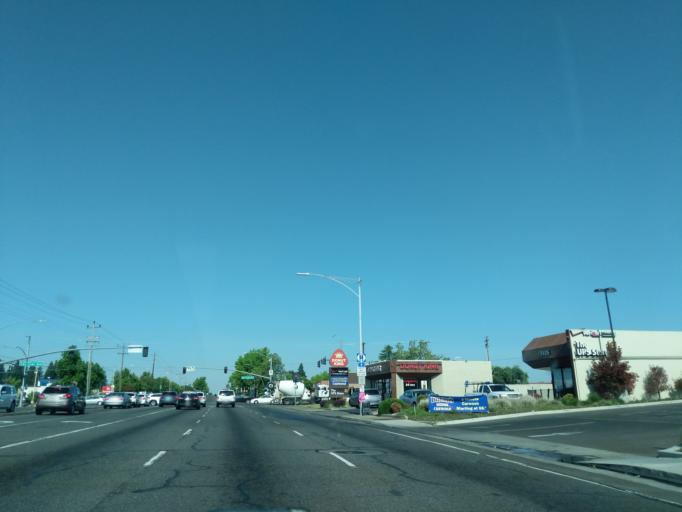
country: US
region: California
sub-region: Sacramento County
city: Citrus Heights
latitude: 38.6784
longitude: -121.2913
